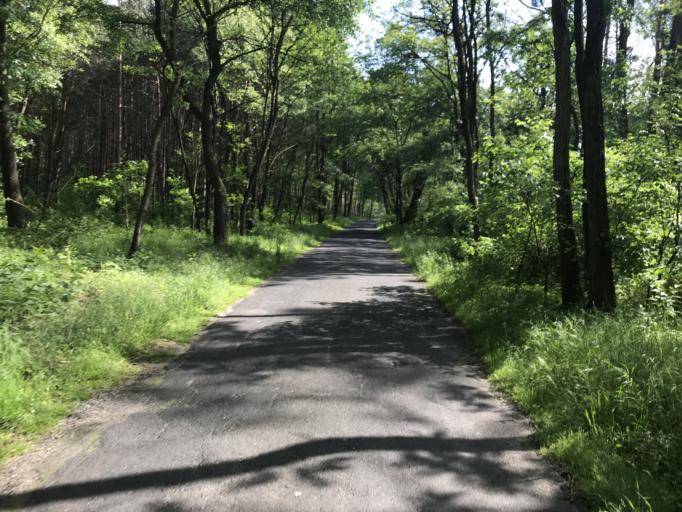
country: PL
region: West Pomeranian Voivodeship
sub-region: Powiat mysliborski
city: Debno
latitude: 52.8270
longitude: 14.7462
